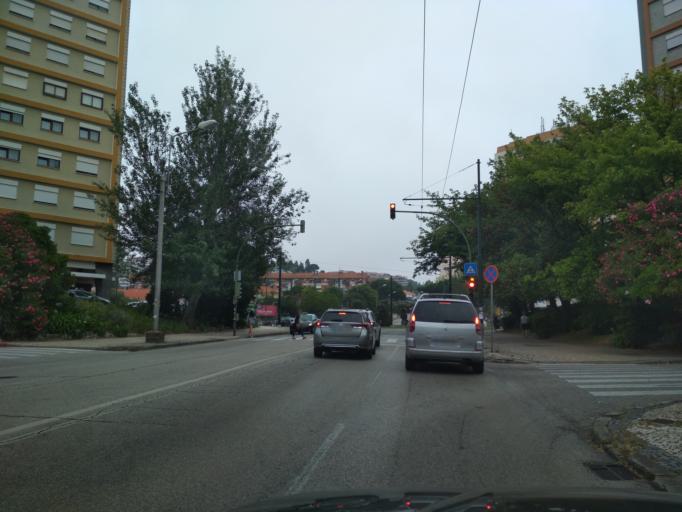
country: PT
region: Coimbra
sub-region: Coimbra
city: Coimbra
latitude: 40.2041
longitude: -8.4042
